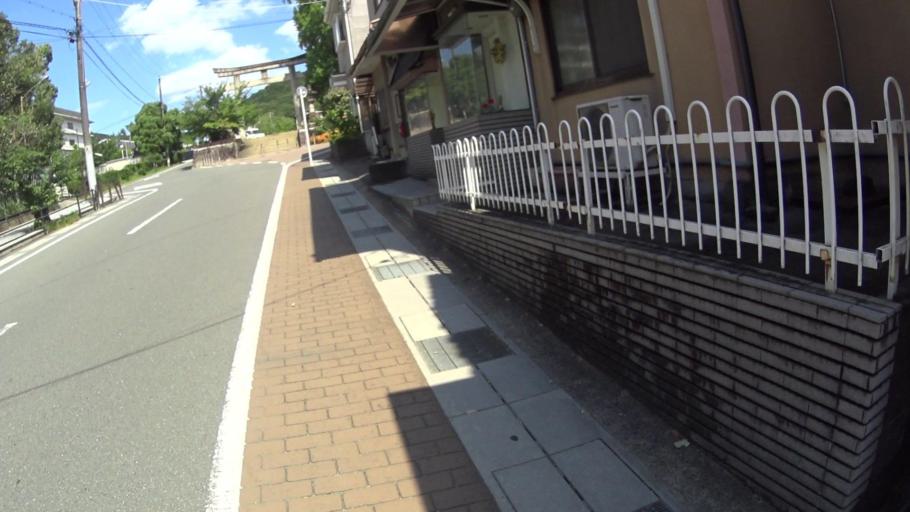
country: RU
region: Rostov
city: Remontnoye
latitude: 46.4986
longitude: 43.7807
